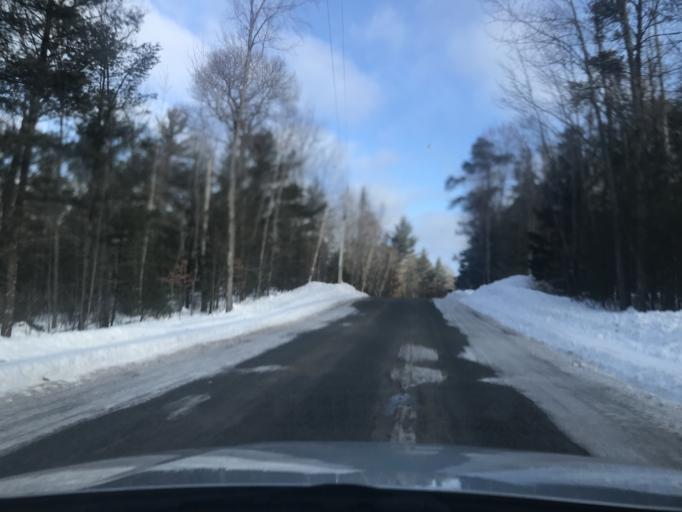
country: US
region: Wisconsin
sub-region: Marinette County
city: Niagara
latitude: 45.6310
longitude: -87.9680
